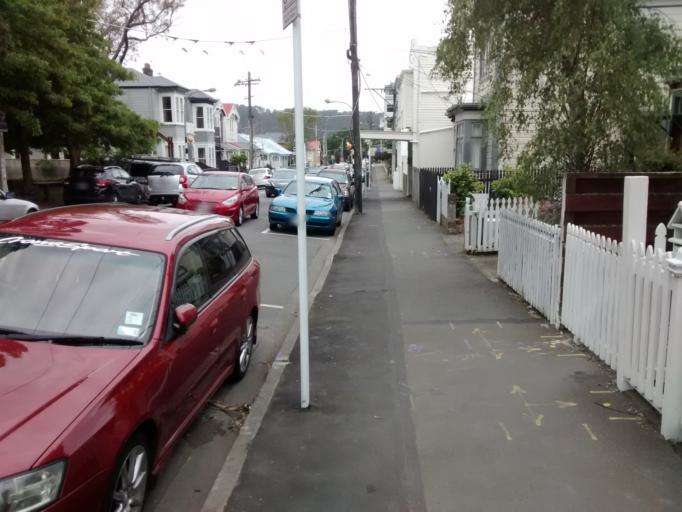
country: NZ
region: Wellington
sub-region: Wellington City
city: Wellington
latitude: -41.2955
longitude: 174.7680
